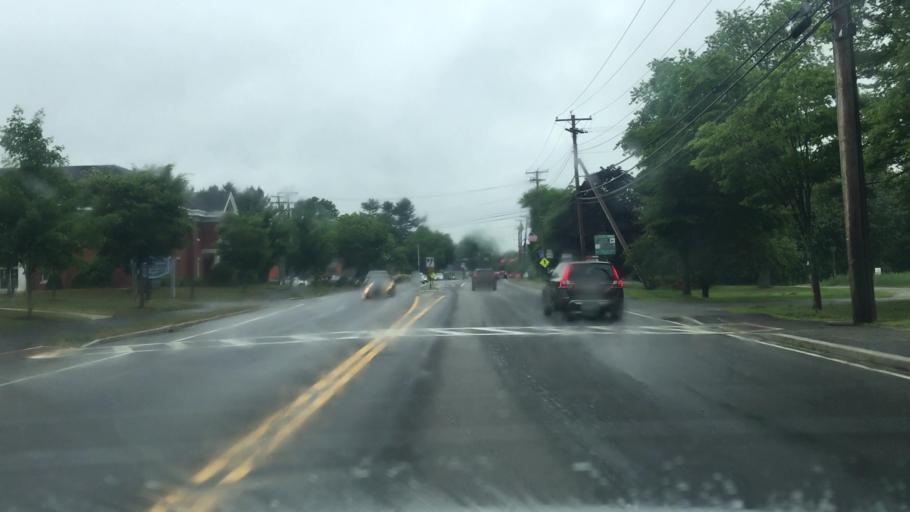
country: US
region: Maine
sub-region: Sagadahoc County
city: Topsham
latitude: 43.9346
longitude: -69.9657
